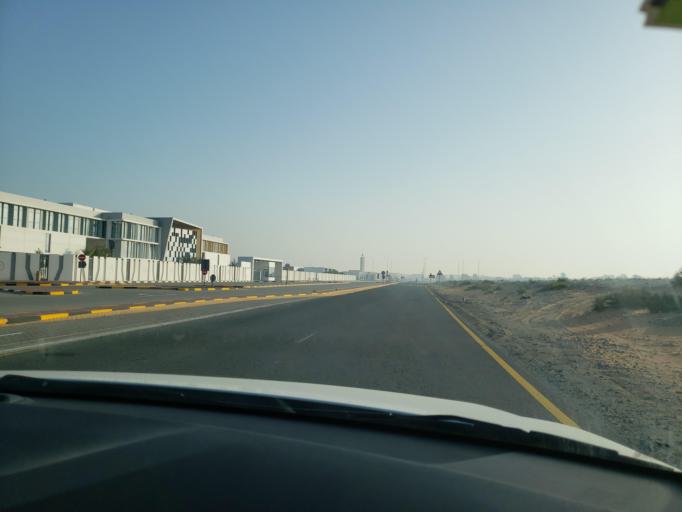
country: AE
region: Umm al Qaywayn
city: Umm al Qaywayn
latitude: 25.4665
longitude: 55.6117
